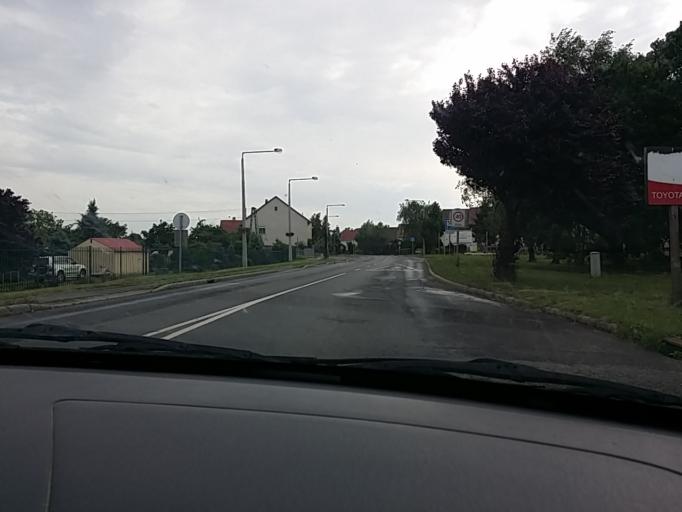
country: HU
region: Borsod-Abauj-Zemplen
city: Tokaj
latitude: 48.1063
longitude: 21.4011
